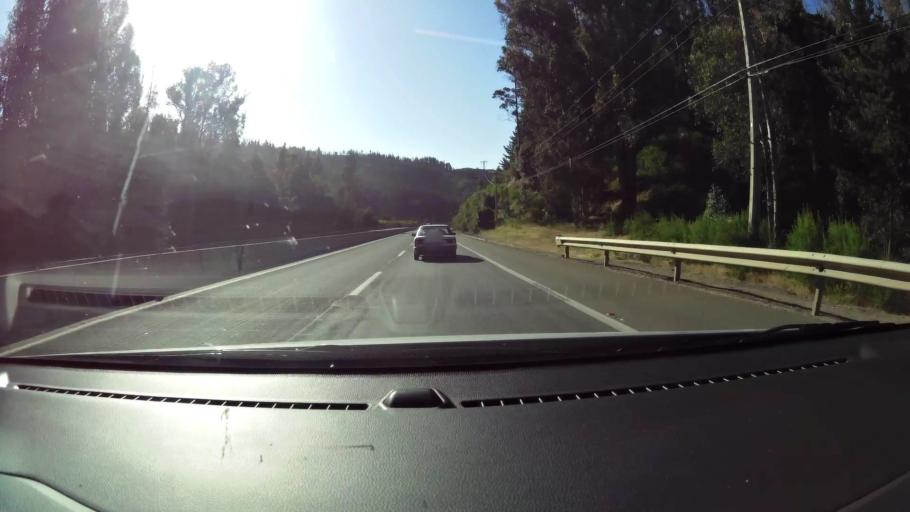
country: CL
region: Valparaiso
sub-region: Provincia de Valparaiso
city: Vina del Mar
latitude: -33.0884
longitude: -71.5564
